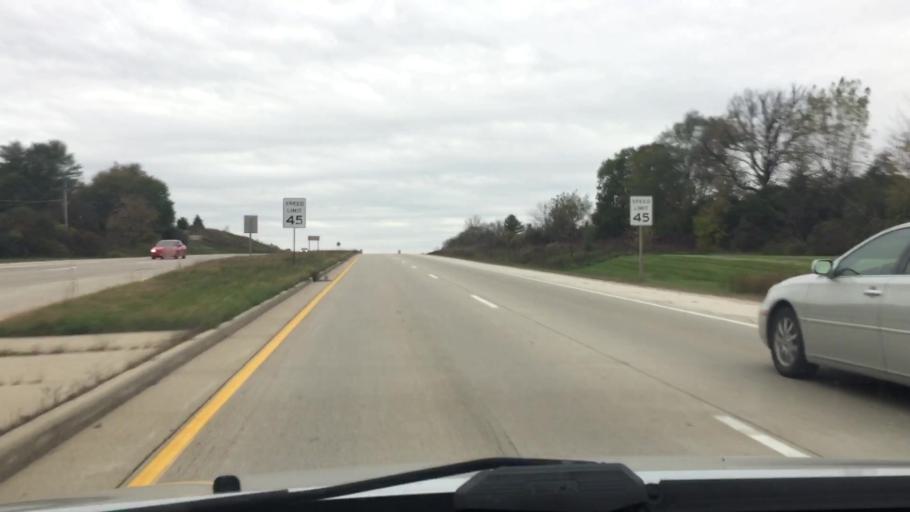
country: US
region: Wisconsin
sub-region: Waukesha County
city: Waukesha
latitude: 42.9770
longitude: -88.2486
